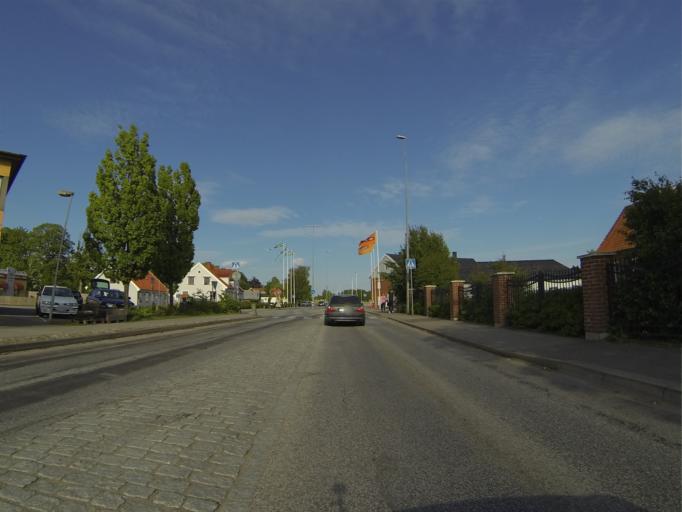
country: SE
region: Skane
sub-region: Staffanstorps Kommun
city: Staffanstorp
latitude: 55.6408
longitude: 13.2132
